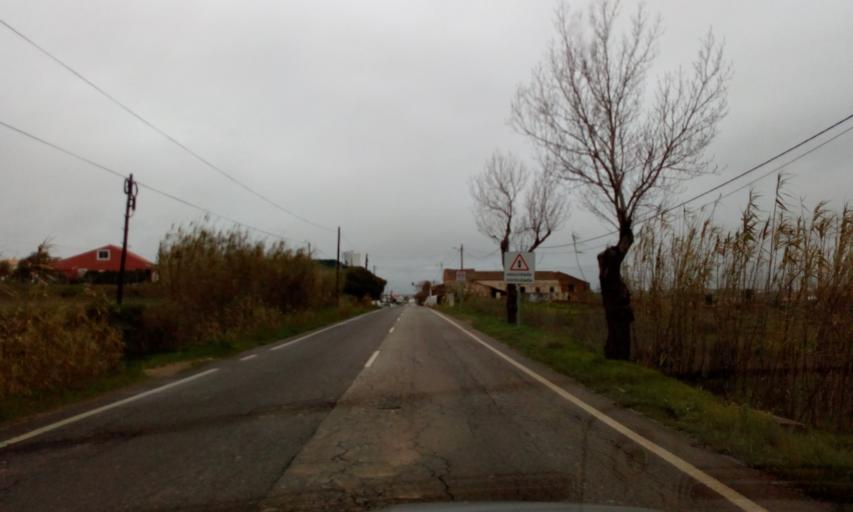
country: PT
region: Faro
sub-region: Albufeira
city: Guia
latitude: 37.1566
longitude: -8.2882
